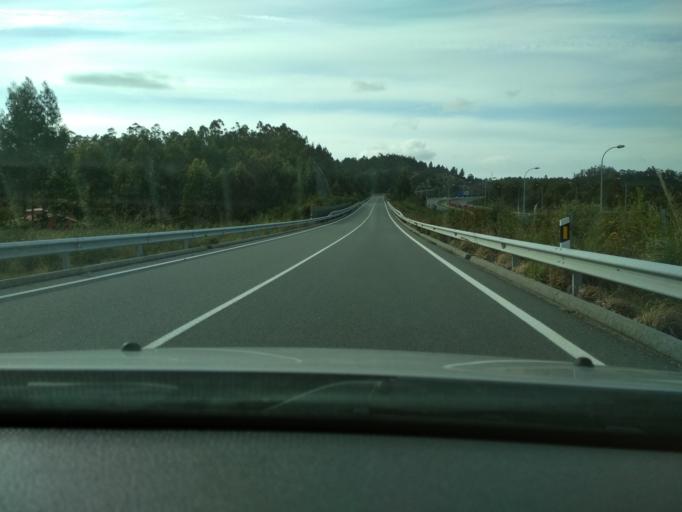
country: ES
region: Galicia
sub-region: Provincia da Coruna
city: Culleredo
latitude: 43.2851
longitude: -8.3971
